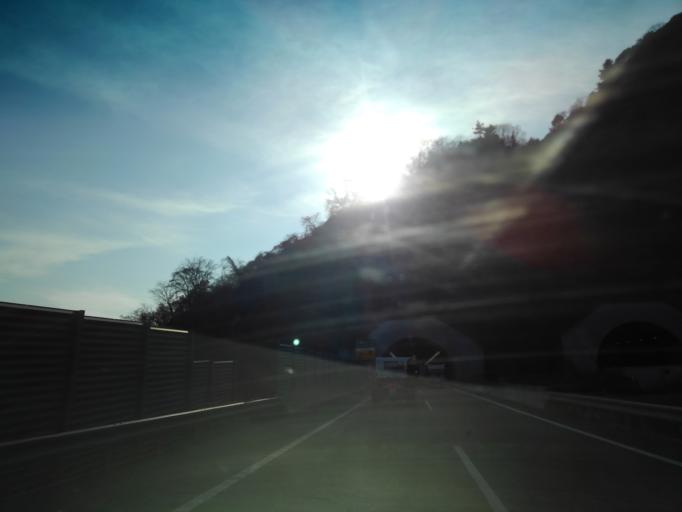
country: JP
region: Tokyo
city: Hachioji
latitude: 35.5760
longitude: 139.2987
